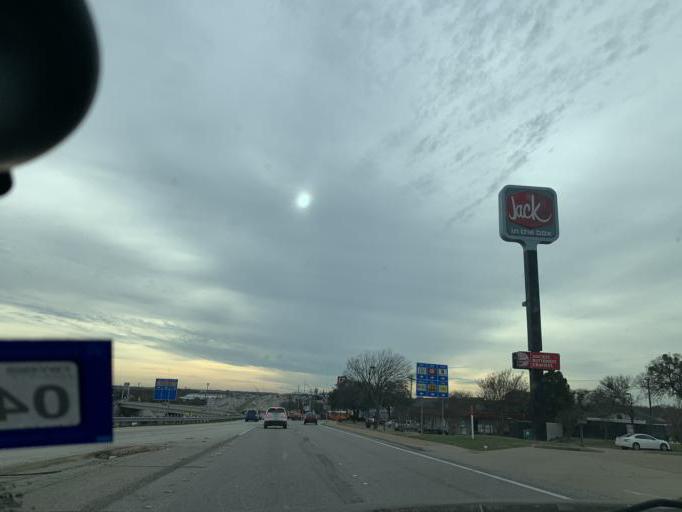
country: US
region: Texas
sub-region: Dallas County
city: Duncanville
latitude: 32.6431
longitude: -96.8901
